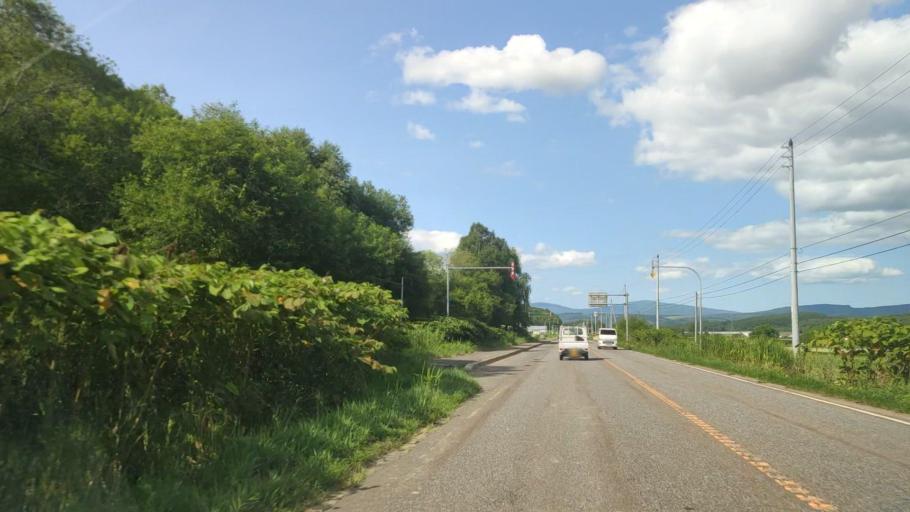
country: JP
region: Hokkaido
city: Nayoro
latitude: 44.3974
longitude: 142.3947
